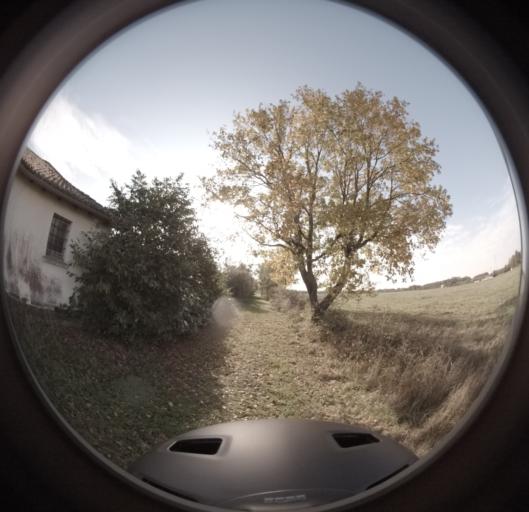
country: FR
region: Midi-Pyrenees
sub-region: Departement du Tarn-et-Garonne
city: Montbeton
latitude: 43.9906
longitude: 1.2881
